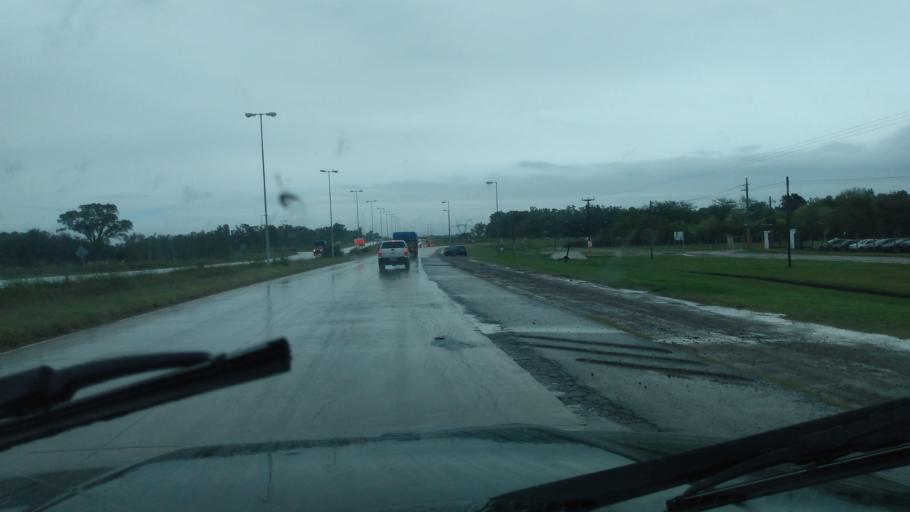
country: AR
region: Buenos Aires
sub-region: Partido de Pilar
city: Pilar
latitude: -34.3919
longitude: -59.0199
